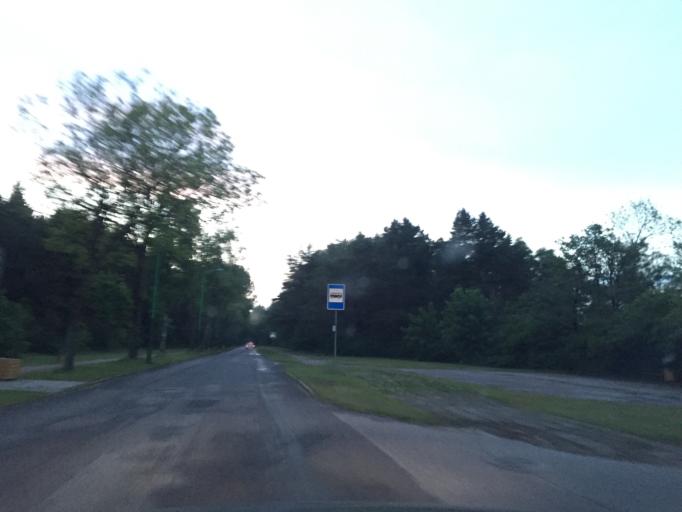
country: LT
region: Klaipedos apskritis
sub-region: Klaipeda
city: Palanga
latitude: 55.8948
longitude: 21.0615
